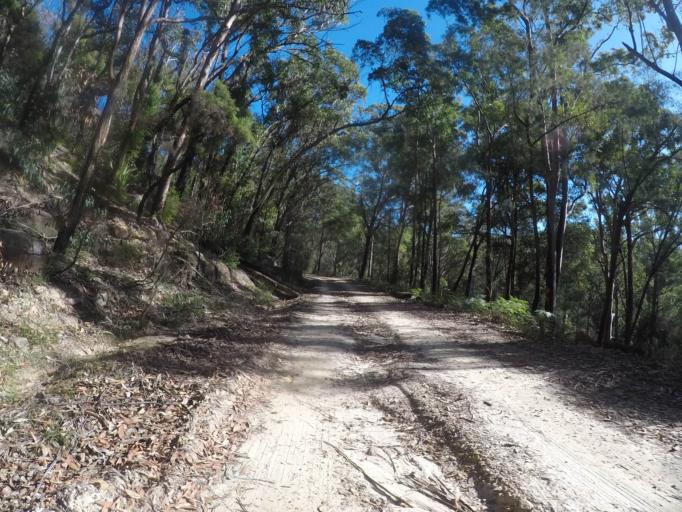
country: AU
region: New South Wales
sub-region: Gosford Shire
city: Point Clare
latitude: -33.3348
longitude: 151.0755
